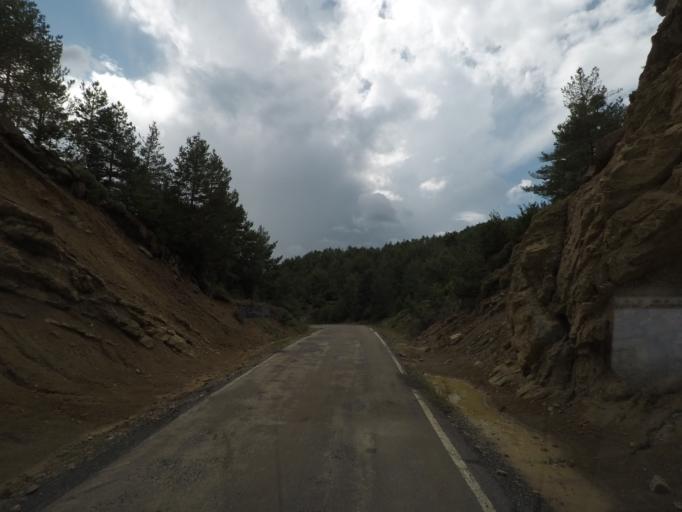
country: ES
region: Aragon
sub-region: Provincia de Huesca
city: Boltana
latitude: 42.4015
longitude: -0.0301
